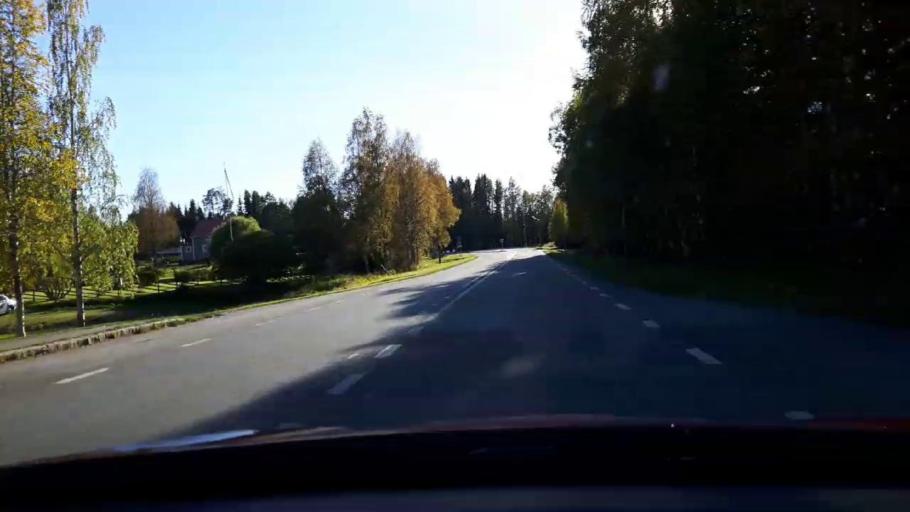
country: SE
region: Jaemtland
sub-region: Stroemsunds Kommun
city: Stroemsund
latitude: 63.8434
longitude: 15.5284
